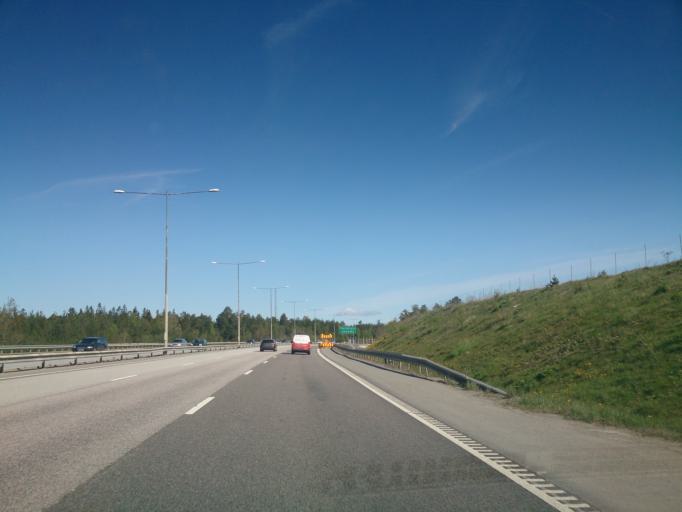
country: SE
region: Stockholm
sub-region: Haninge Kommun
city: Handen
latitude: 59.2083
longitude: 18.1306
